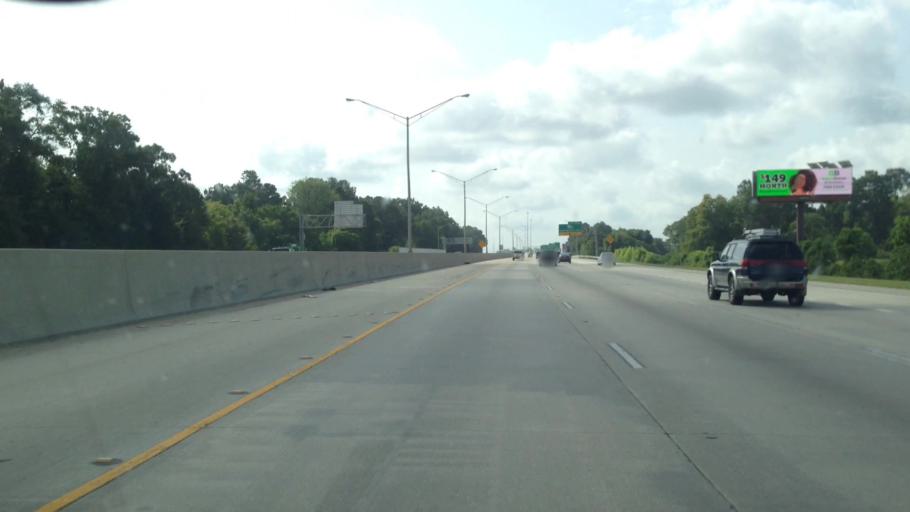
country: US
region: Louisiana
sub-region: East Baton Rouge Parish
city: Inniswold
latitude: 30.4029
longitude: -91.0955
